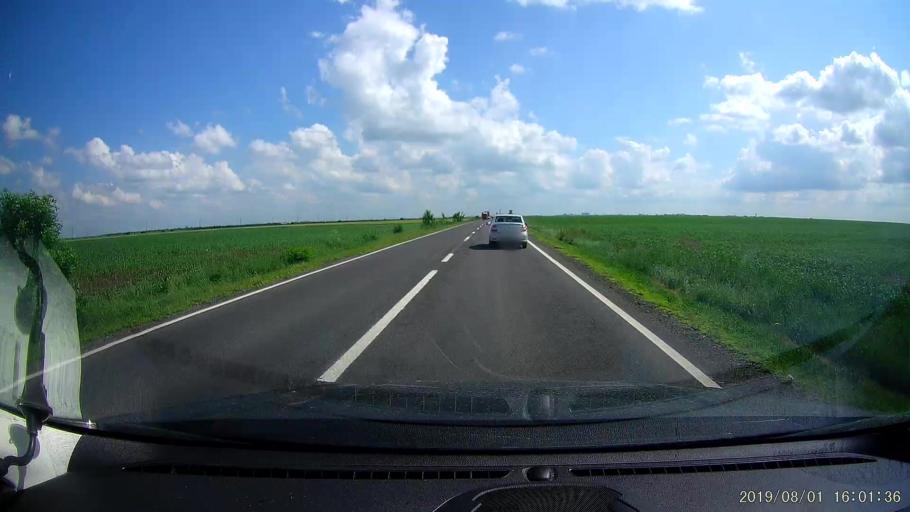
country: RO
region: Ialomita
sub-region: Comuna Ciulnita
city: Ciulnita
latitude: 44.5053
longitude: 27.3899
